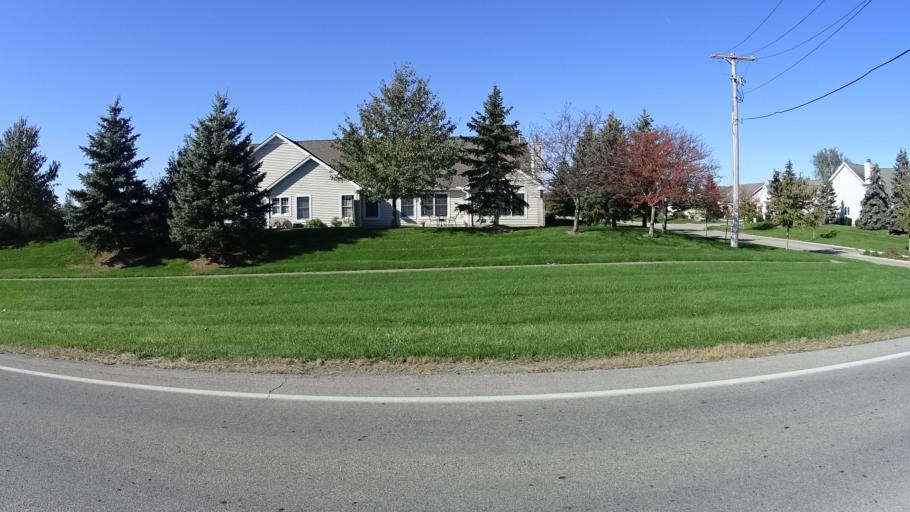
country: US
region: Ohio
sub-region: Lorain County
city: Oberlin
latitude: 41.2740
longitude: -82.2173
